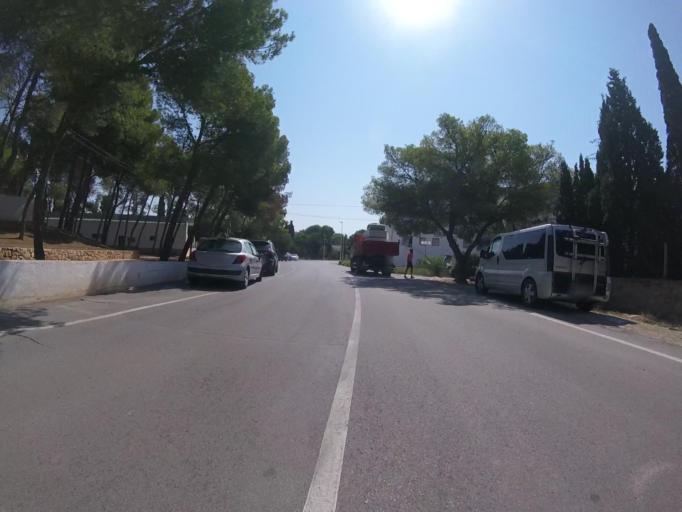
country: ES
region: Valencia
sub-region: Provincia de Castello
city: Alcoceber
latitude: 40.2500
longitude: 0.2830
